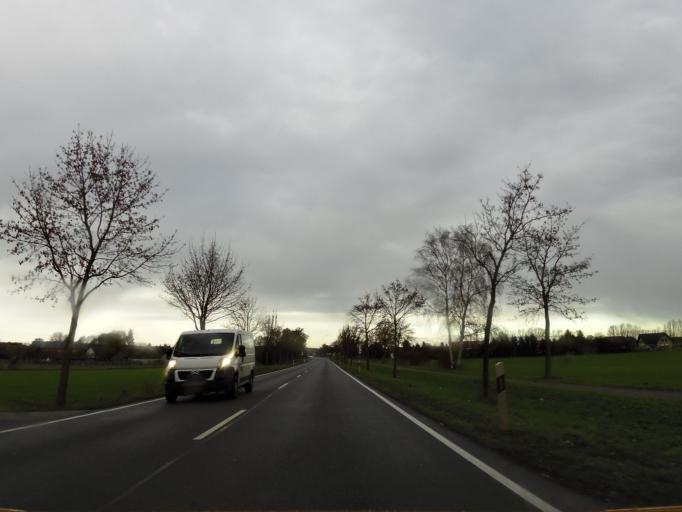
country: DE
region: Saxony-Anhalt
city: Gardelegen
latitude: 52.5405
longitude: 11.3707
